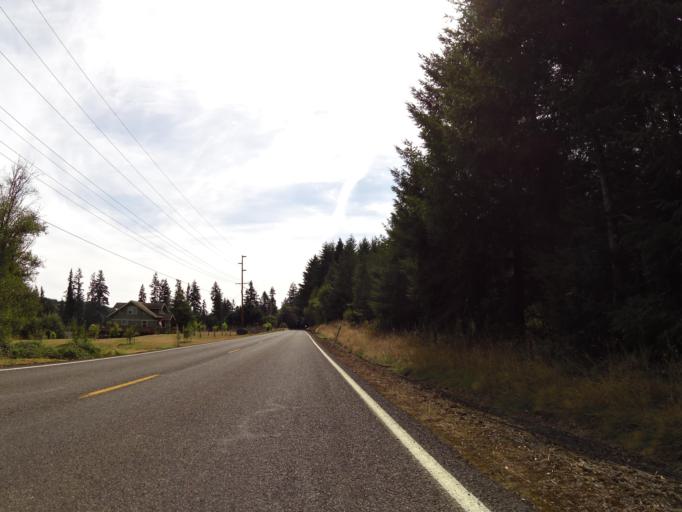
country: US
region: Washington
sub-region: Lewis County
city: Winlock
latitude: 46.4364
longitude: -122.9701
